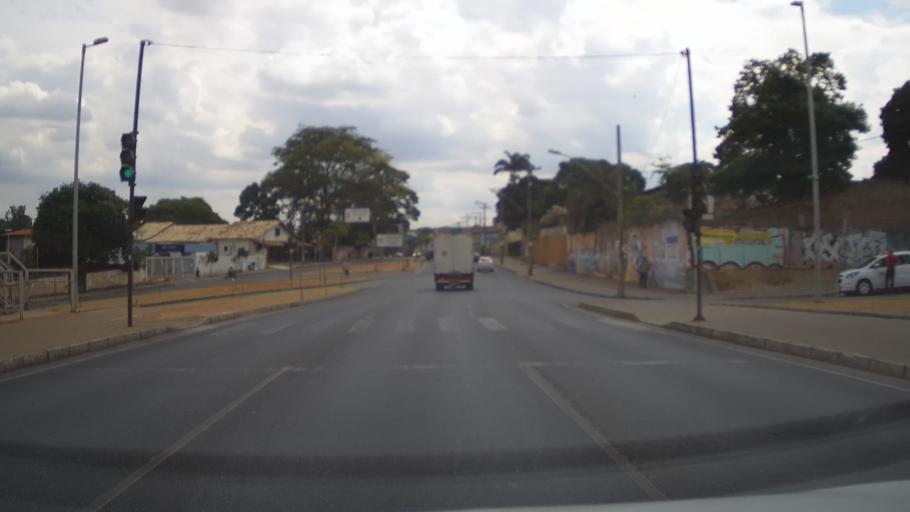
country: BR
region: Minas Gerais
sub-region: Belo Horizonte
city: Belo Horizonte
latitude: -19.8420
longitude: -43.9684
